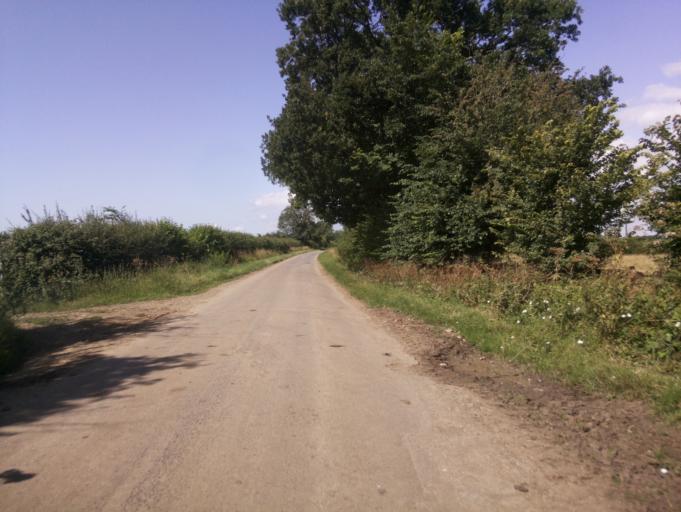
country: GB
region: England
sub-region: Milton Keynes
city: Calverton
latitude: 51.9962
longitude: -0.8768
